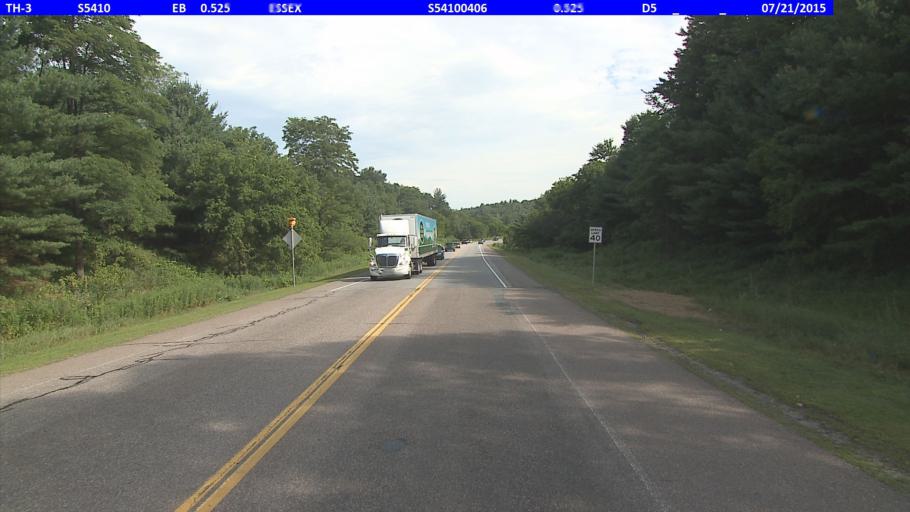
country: US
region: Vermont
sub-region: Chittenden County
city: Essex Junction
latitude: 44.5104
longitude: -73.1316
